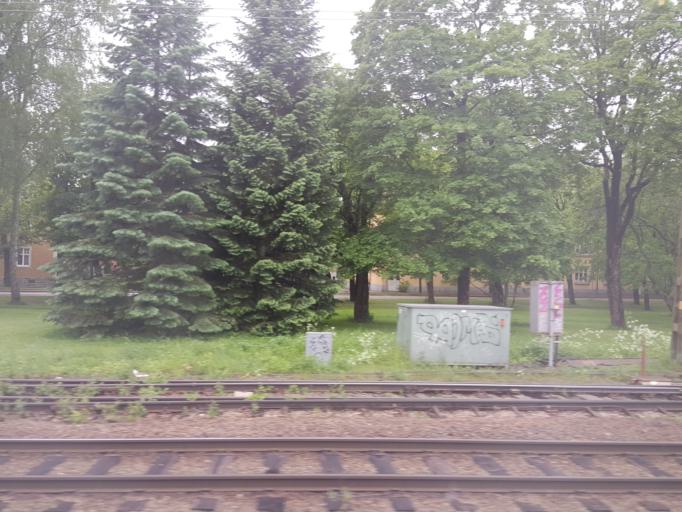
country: SE
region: Vaestmanland
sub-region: Sala Kommun
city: Sala
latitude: 59.9245
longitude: 16.6089
